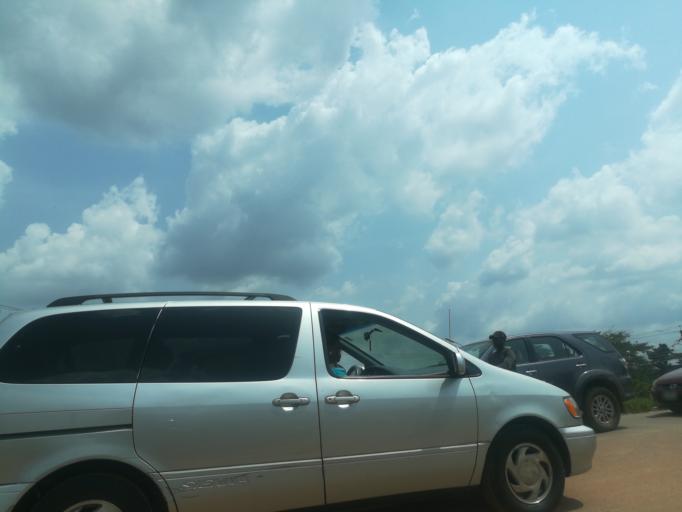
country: NG
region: Oyo
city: Ibadan
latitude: 7.4254
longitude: 3.9374
